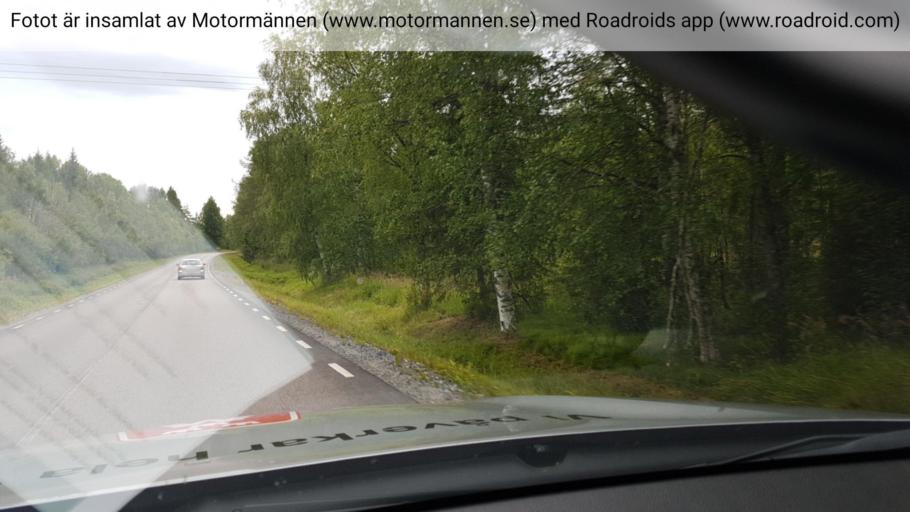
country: SE
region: Norrbotten
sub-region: Lulea Kommun
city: Gammelstad
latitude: 65.6527
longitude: 22.0334
